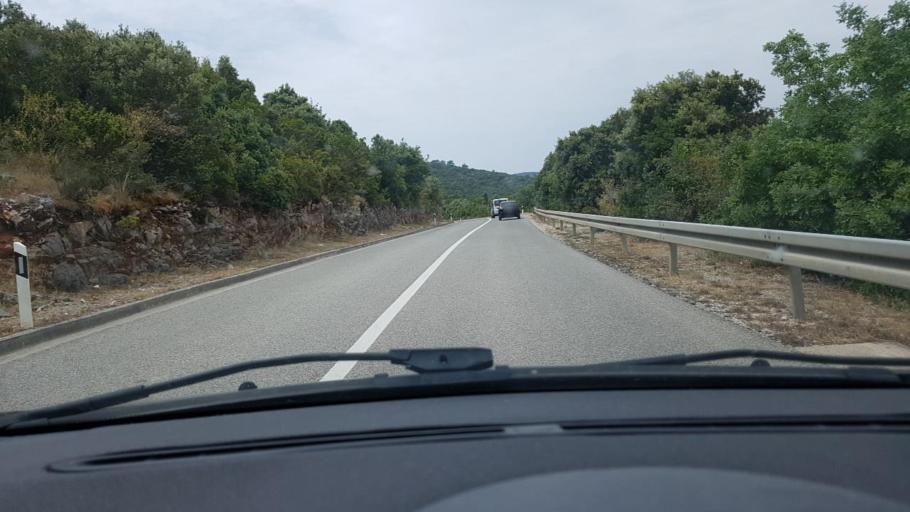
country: HR
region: Dubrovacko-Neretvanska
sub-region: Grad Korcula
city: Zrnovo
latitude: 42.9401
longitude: 17.0627
